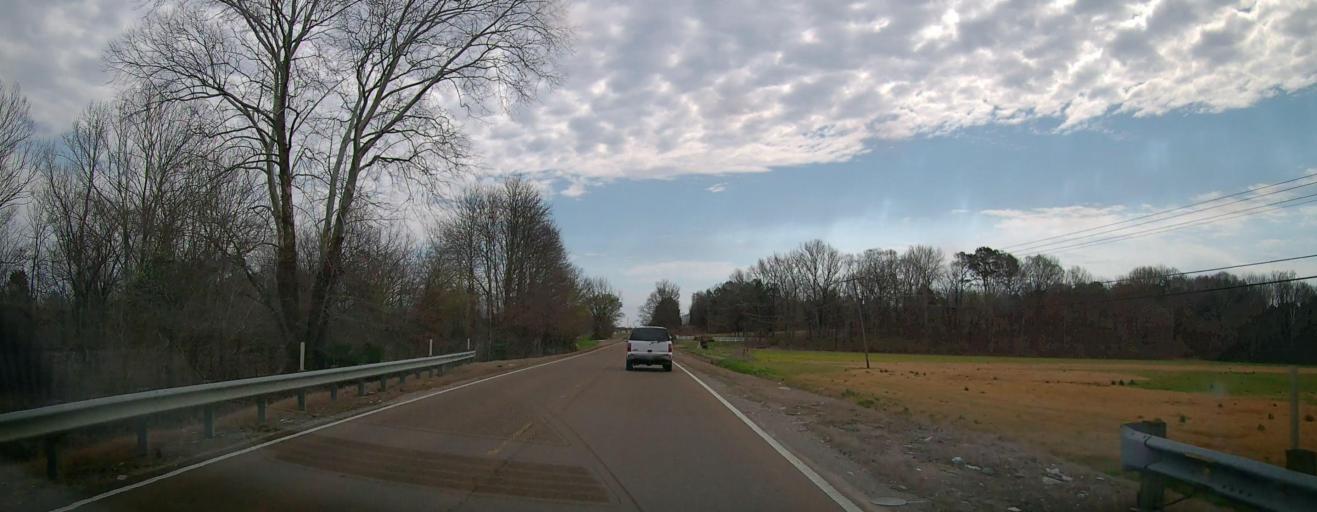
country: US
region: Mississippi
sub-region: Marshall County
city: Byhalia
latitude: 34.8704
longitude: -89.6766
